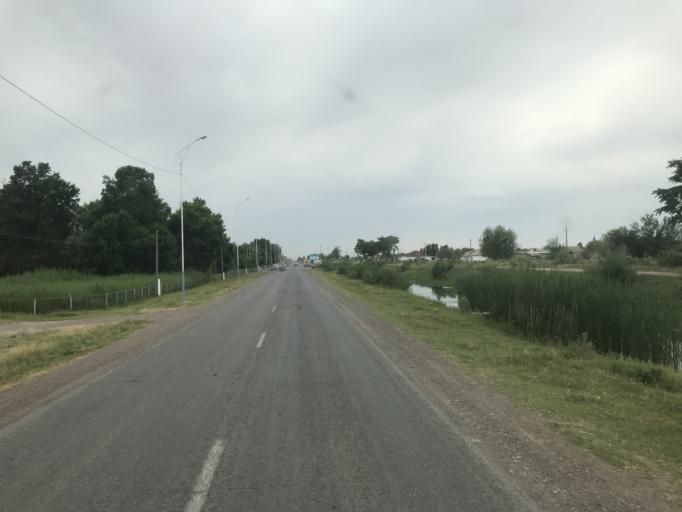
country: KZ
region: Ongtustik Qazaqstan
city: Asykata
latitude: 40.9370
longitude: 68.4115
